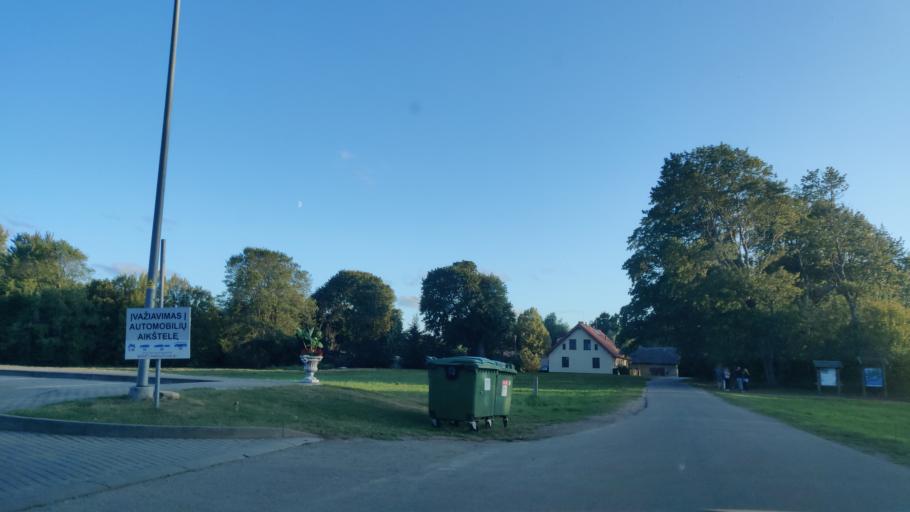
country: LT
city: Neringa
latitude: 55.3452
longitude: 21.1936
